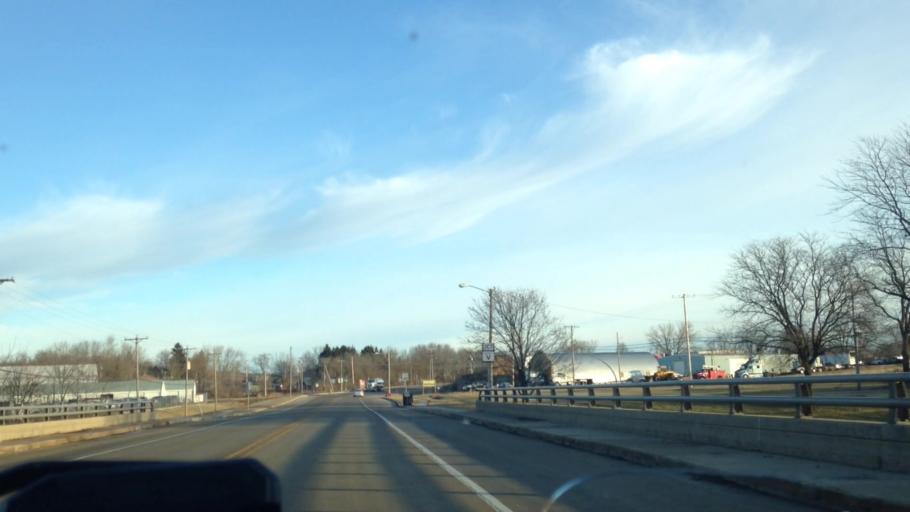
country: US
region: Wisconsin
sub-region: Dodge County
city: Mayville
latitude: 43.5069
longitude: -88.5421
